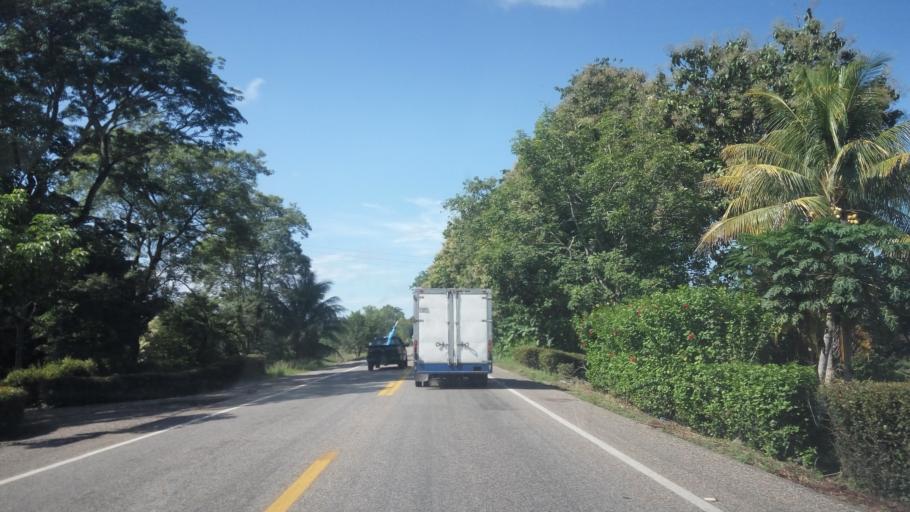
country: MX
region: Tabasco
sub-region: Teapa
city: Eureka y Belen
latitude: 17.6709
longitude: -92.9492
